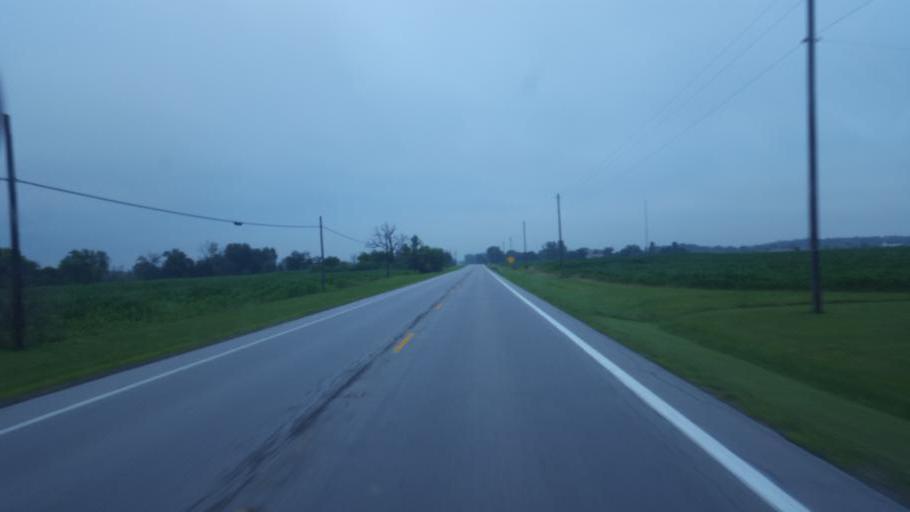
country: US
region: Ohio
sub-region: Madison County
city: Mount Sterling
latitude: 39.6855
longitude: -83.2972
